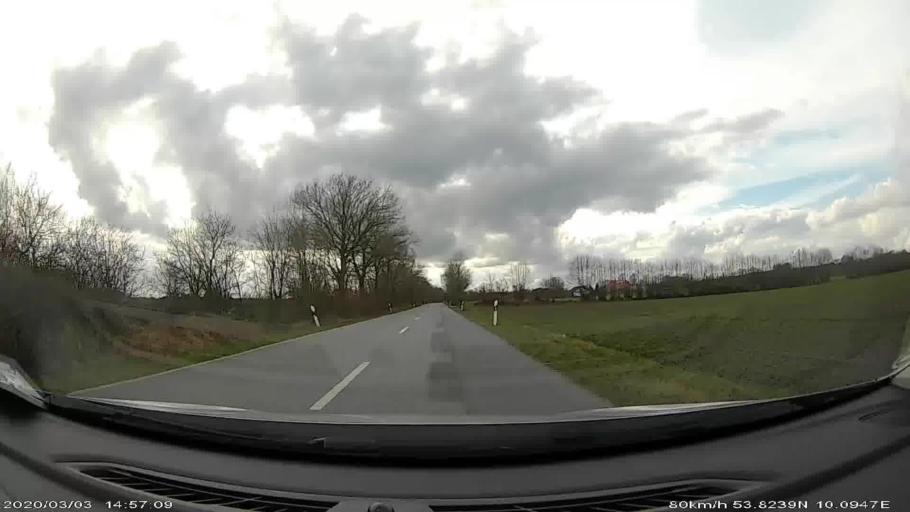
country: DE
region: Schleswig-Holstein
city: Sievershutten
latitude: 53.8242
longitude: 10.0952
